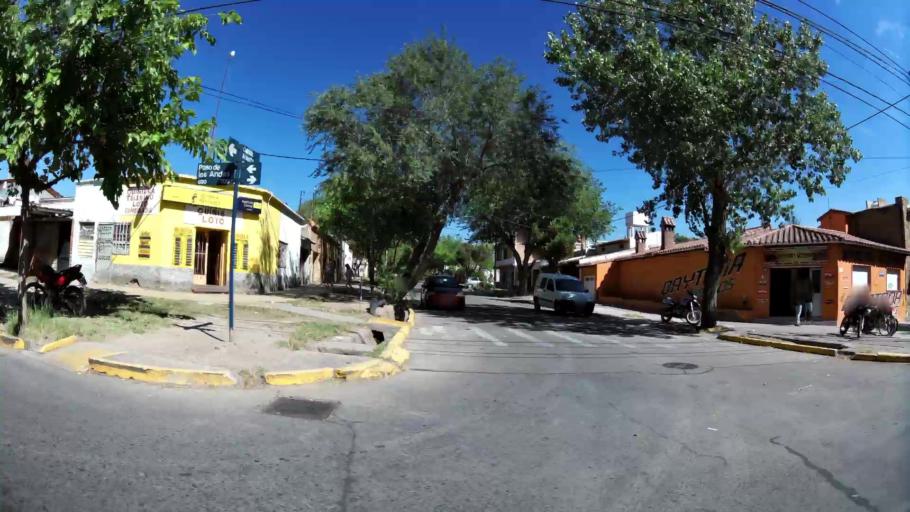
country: AR
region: Mendoza
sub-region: Departamento de Godoy Cruz
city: Godoy Cruz
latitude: -32.9183
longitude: -68.8595
